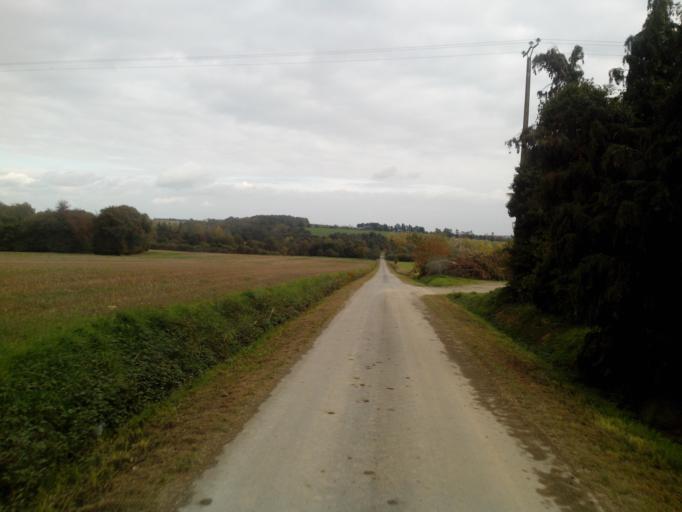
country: FR
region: Brittany
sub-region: Departement du Morbihan
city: Mauron
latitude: 48.0616
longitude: -2.3368
